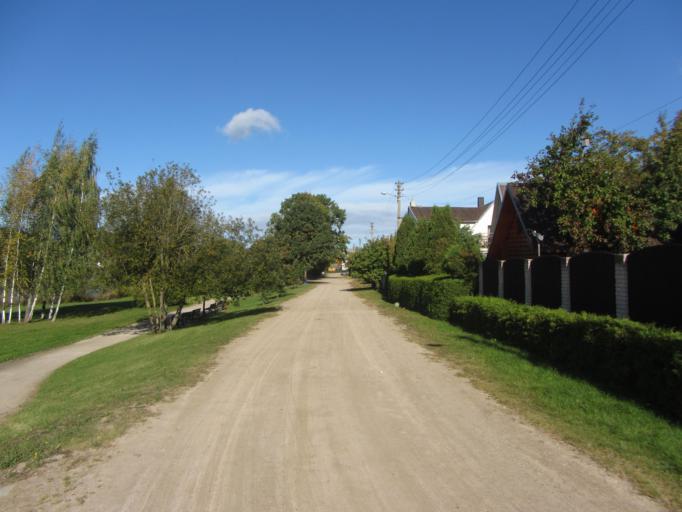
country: LT
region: Utenos apskritis
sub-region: Utena
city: Utena
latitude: 55.5064
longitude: 25.6076
